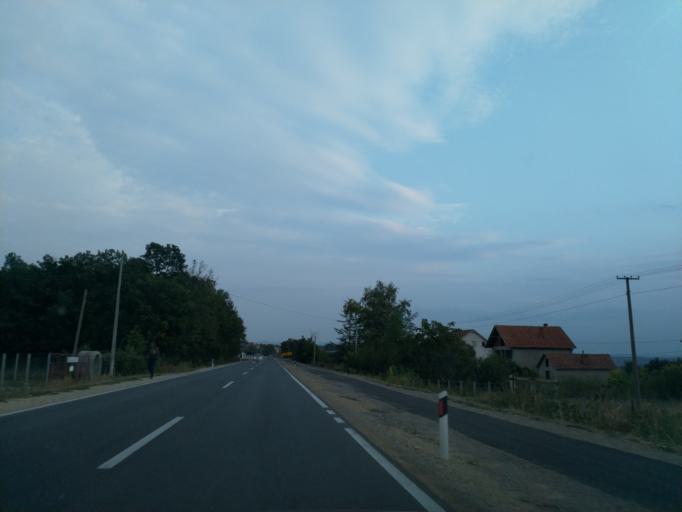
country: RS
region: Central Serbia
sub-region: Sumadijski Okrug
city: Kragujevac
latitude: 44.0864
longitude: 20.8668
